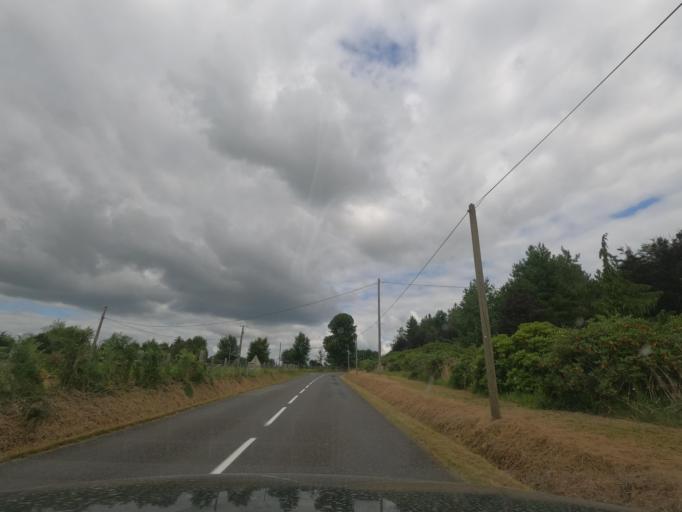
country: FR
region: Lower Normandy
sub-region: Departement de la Manche
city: Le Teilleul
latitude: 48.5048
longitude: -0.9113
